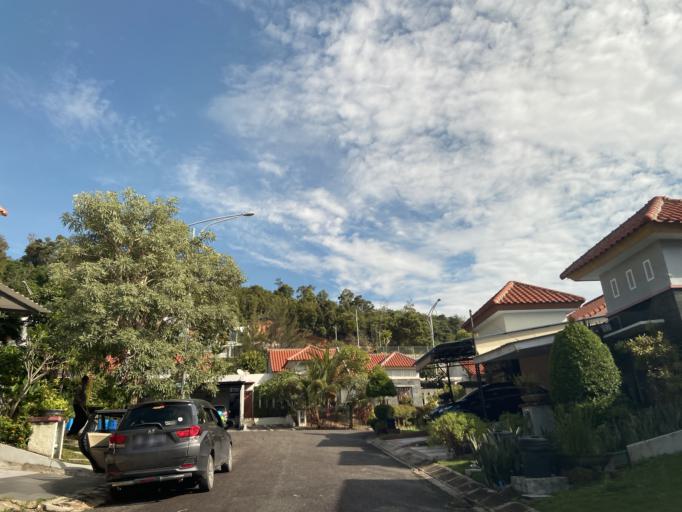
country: SG
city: Singapore
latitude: 1.0958
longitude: 104.0284
